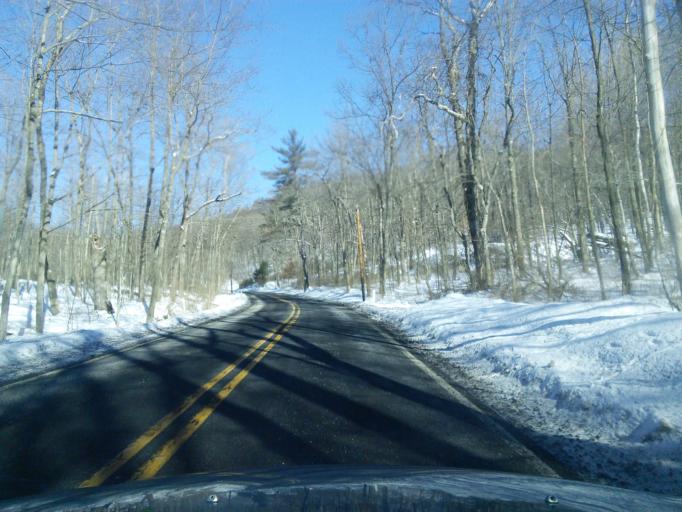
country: US
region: Pennsylvania
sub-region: Centre County
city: Park Forest Village
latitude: 40.8417
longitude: -77.9355
